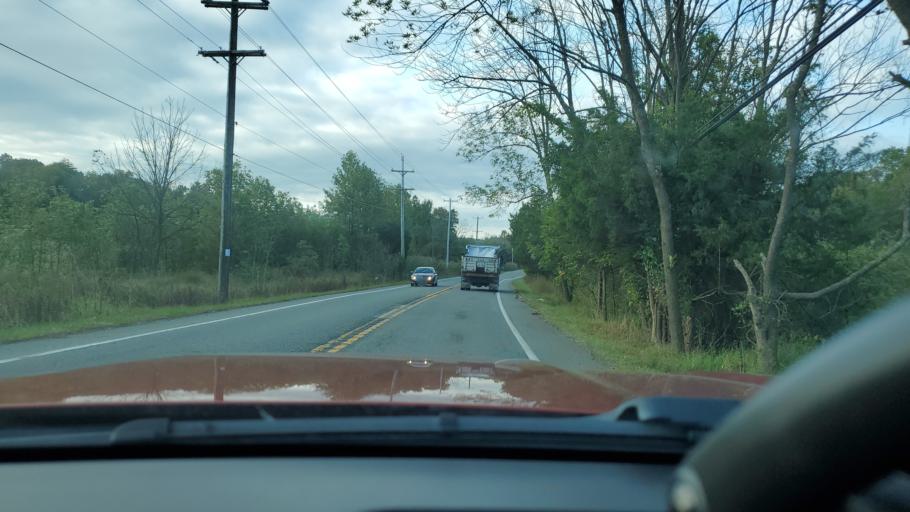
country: US
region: Pennsylvania
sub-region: Montgomery County
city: Woxall
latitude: 40.3147
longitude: -75.4809
